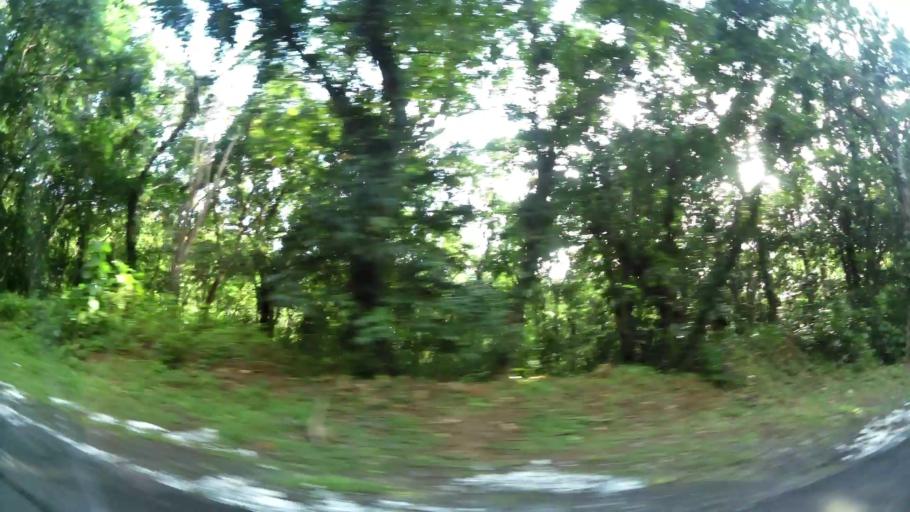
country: GP
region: Guadeloupe
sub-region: Guadeloupe
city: Bouillante
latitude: 16.1817
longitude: -61.7609
